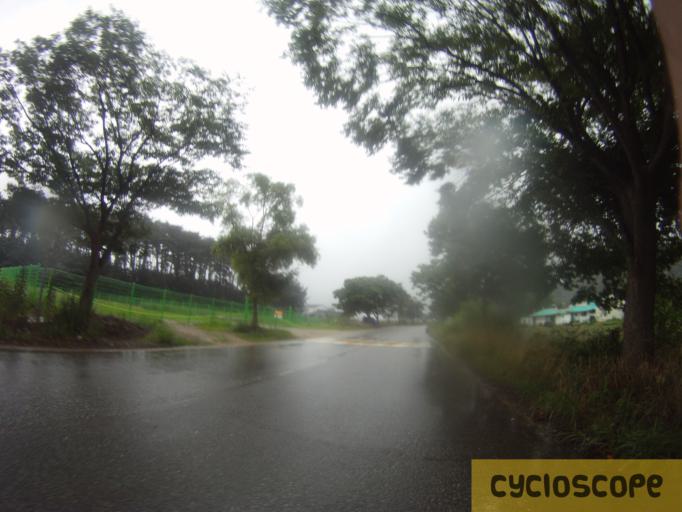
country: KR
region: Gyeonggi-do
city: Hwaseong-si
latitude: 36.9808
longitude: 126.8475
